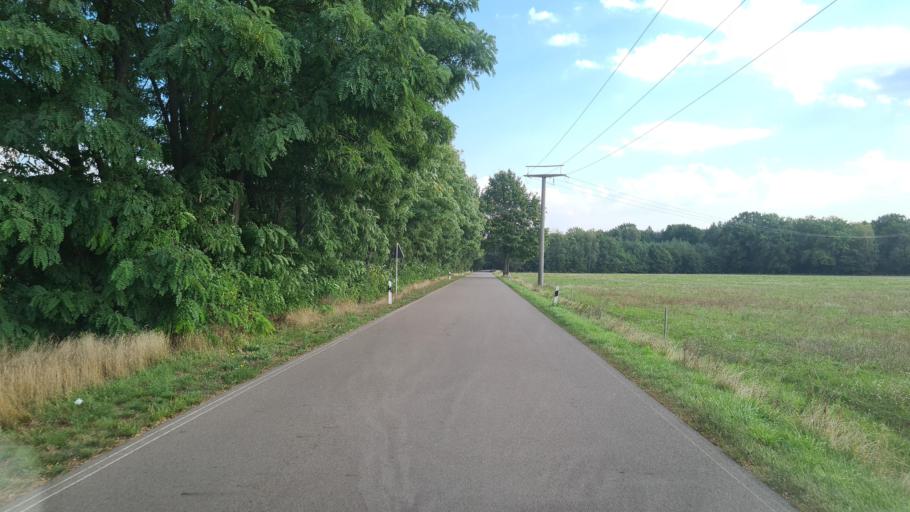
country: DE
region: Brandenburg
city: Drebkau
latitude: 51.6575
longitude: 14.1750
